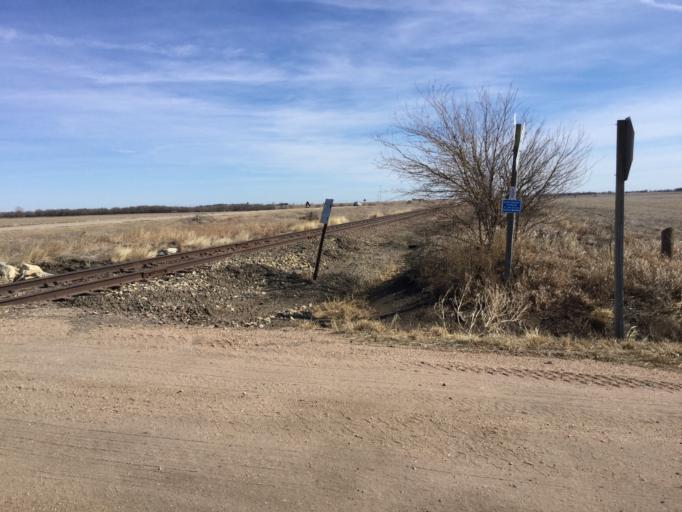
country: US
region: Kansas
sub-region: Rice County
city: Lyons
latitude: 38.5151
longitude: -98.2201
